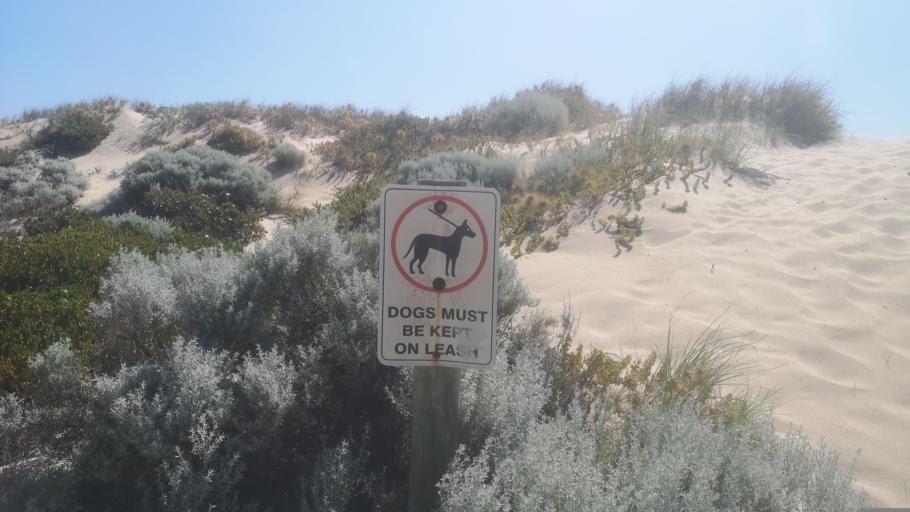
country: AU
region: Western Australia
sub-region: Irwin
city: Dongara
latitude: -29.2613
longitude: 114.9214
